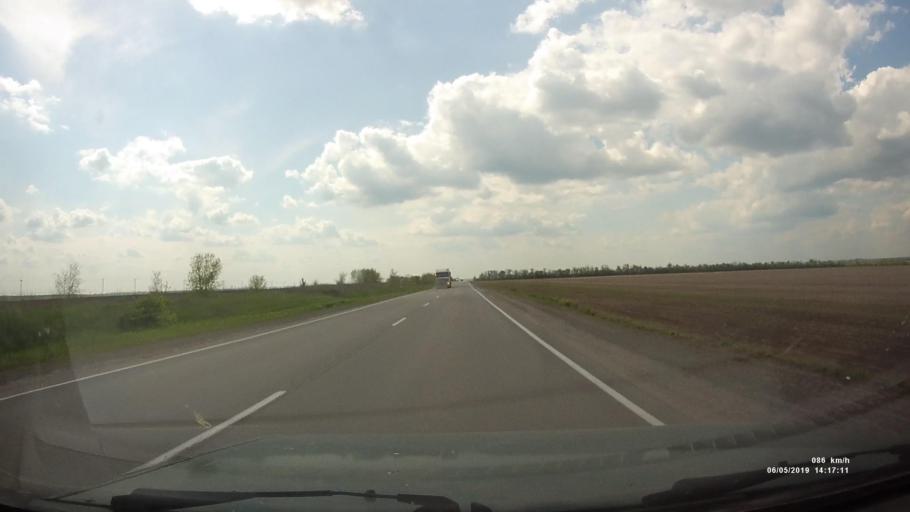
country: RU
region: Rostov
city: Kamenolomni
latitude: 47.6345
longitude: 40.2717
